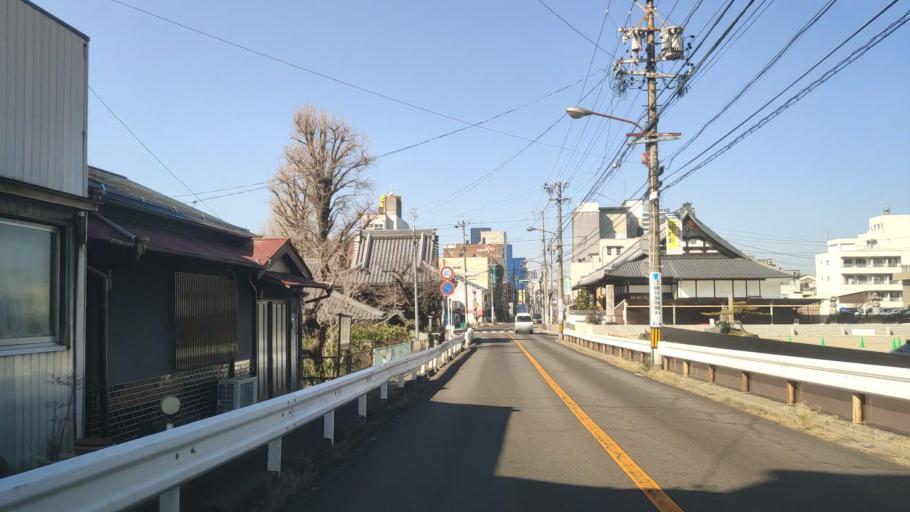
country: JP
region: Gifu
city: Gifu-shi
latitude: 35.4242
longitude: 136.7659
